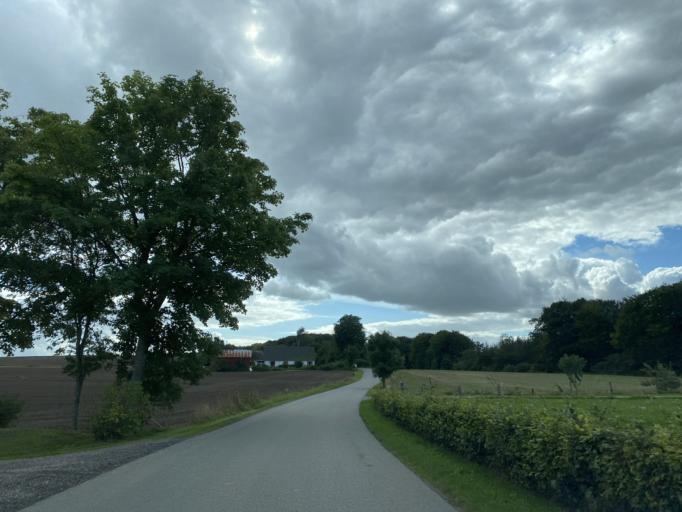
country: DK
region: Central Jutland
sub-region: Horsens Kommune
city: Horsens
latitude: 55.9587
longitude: 9.8581
